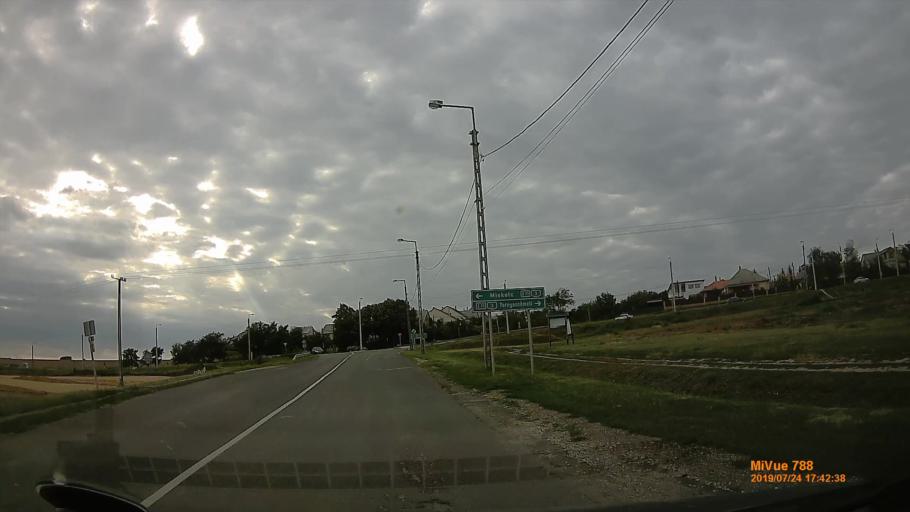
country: HU
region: Borsod-Abauj-Zemplen
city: Encs
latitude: 48.3355
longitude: 21.1082
